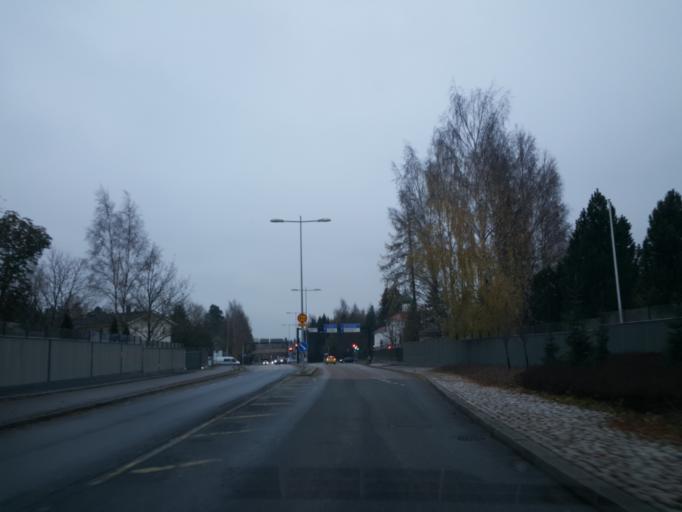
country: FI
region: Uusimaa
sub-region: Helsinki
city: Vantaa
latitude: 60.3010
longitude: 25.0329
